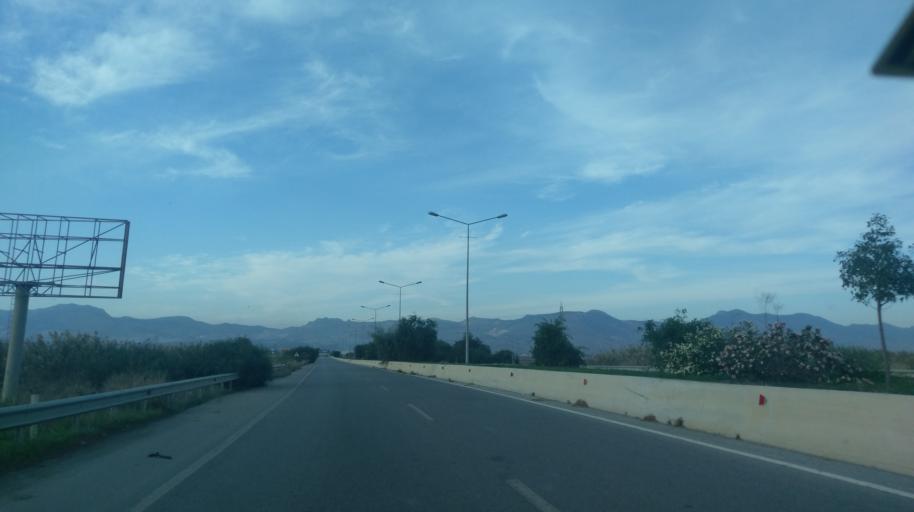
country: CY
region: Lefkosia
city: Geri
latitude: 35.1898
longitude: 33.5026
